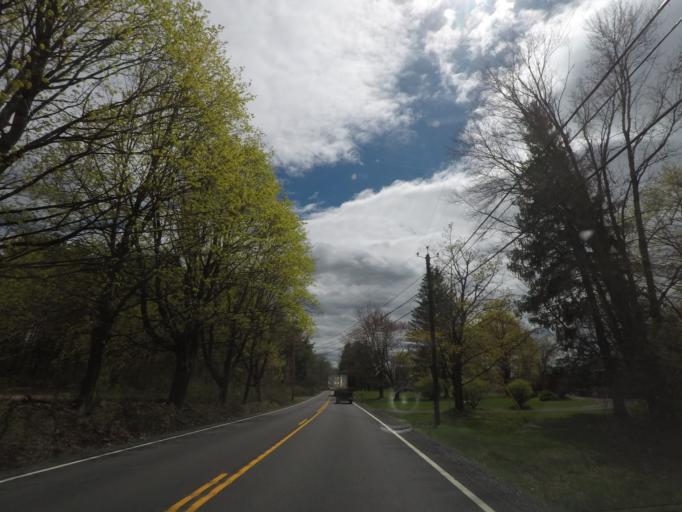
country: US
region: New York
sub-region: Rensselaer County
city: Castleton-on-Hudson
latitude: 42.5195
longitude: -73.7872
